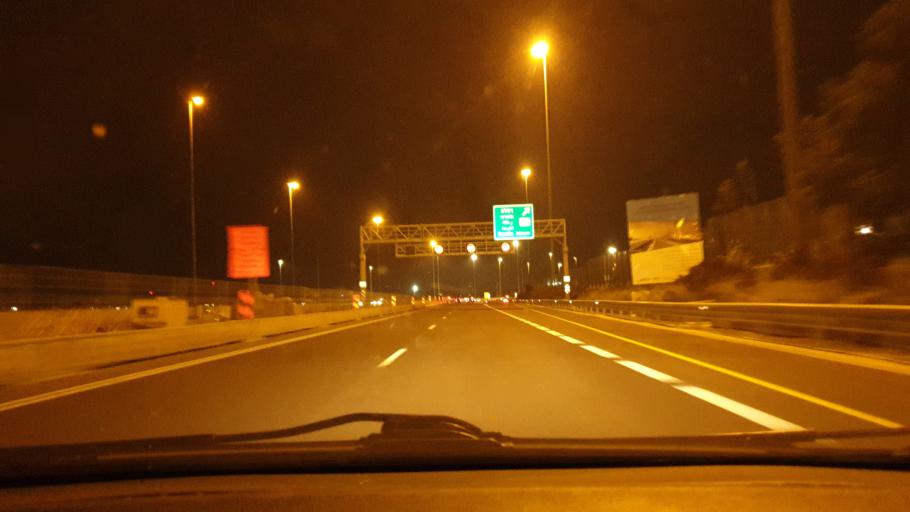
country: IL
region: Central District
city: Ramla
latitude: 31.9206
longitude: 34.8443
